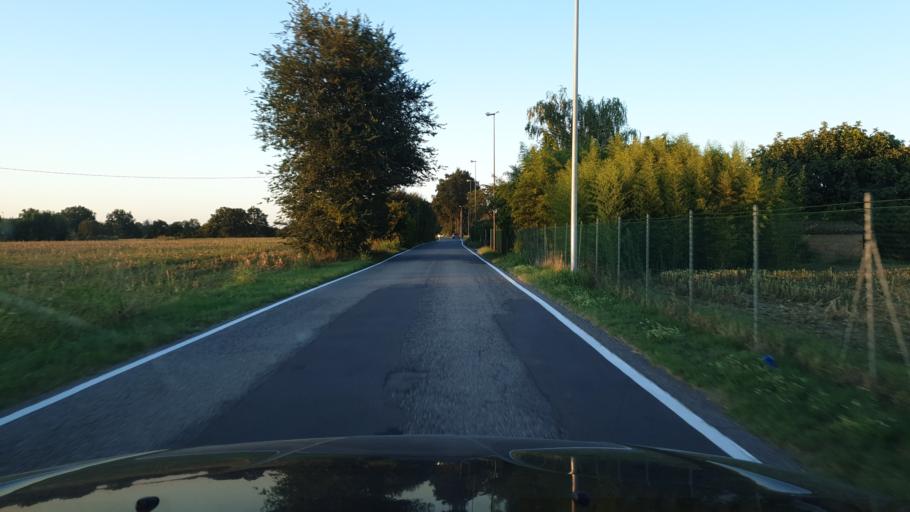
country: IT
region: Emilia-Romagna
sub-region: Provincia di Bologna
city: Quarto Inferiore
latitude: 44.5227
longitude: 11.3913
